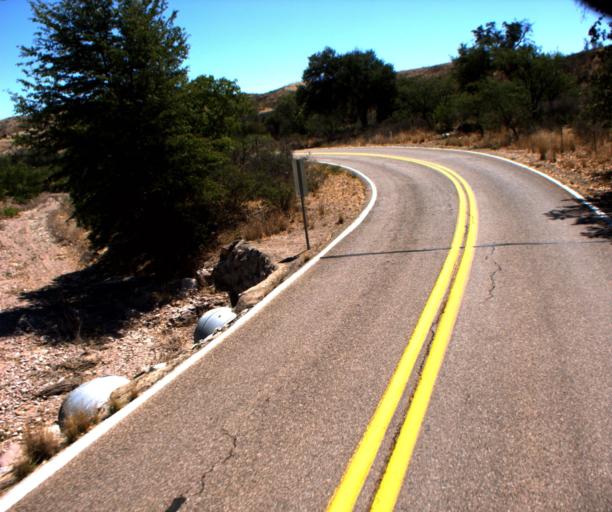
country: US
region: Arizona
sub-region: Santa Cruz County
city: Rio Rico
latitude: 31.3874
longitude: -111.0645
